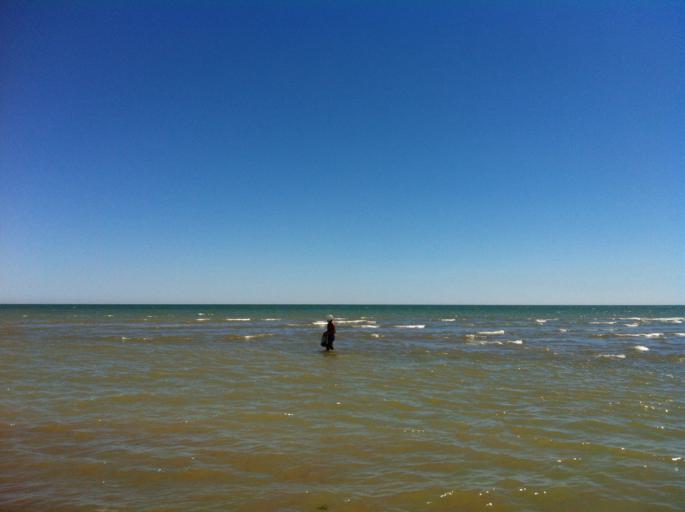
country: IT
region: Apulia
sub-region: Provincia di Foggia
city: Manfredonia
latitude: 41.5869
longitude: 15.8945
